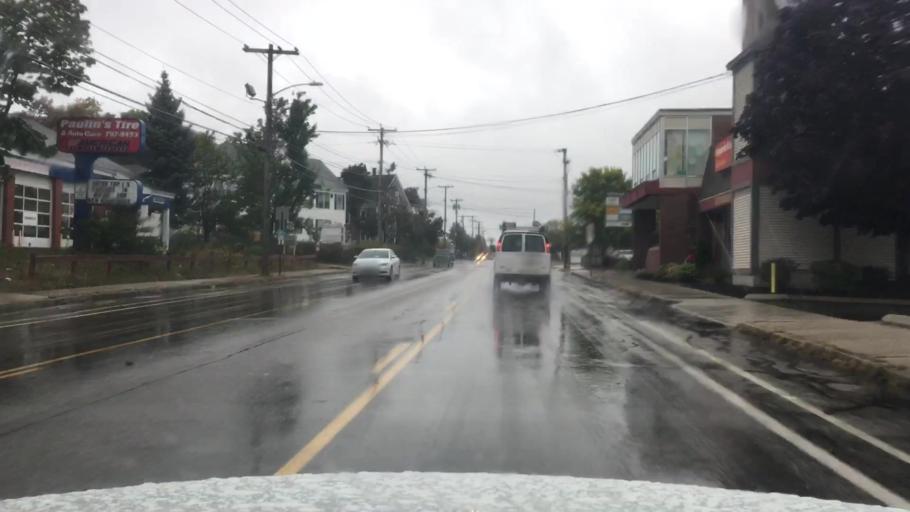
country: US
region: Maine
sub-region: Cumberland County
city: Portland
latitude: 43.6826
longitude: -70.2904
